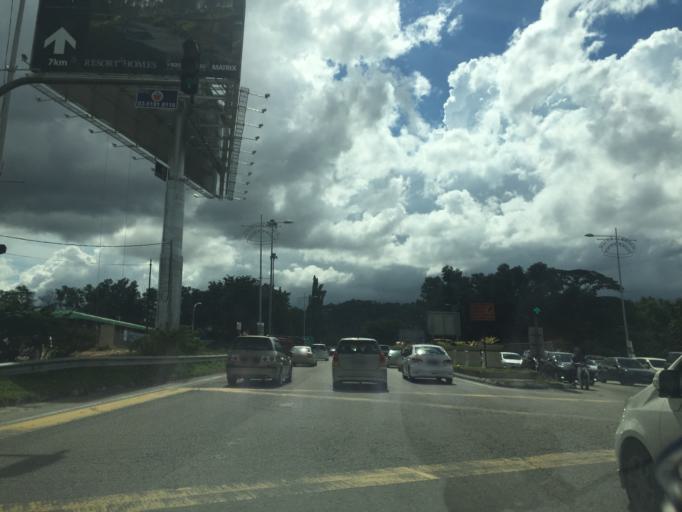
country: MY
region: Negeri Sembilan
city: Seremban
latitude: 2.7162
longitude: 101.9169
